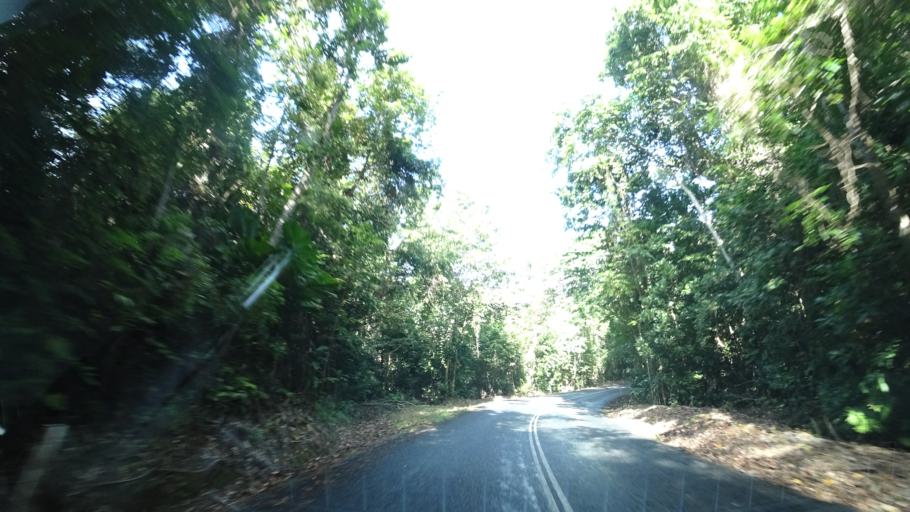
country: AU
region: Queensland
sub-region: Cairns
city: Port Douglas
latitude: -16.1300
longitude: 145.4539
